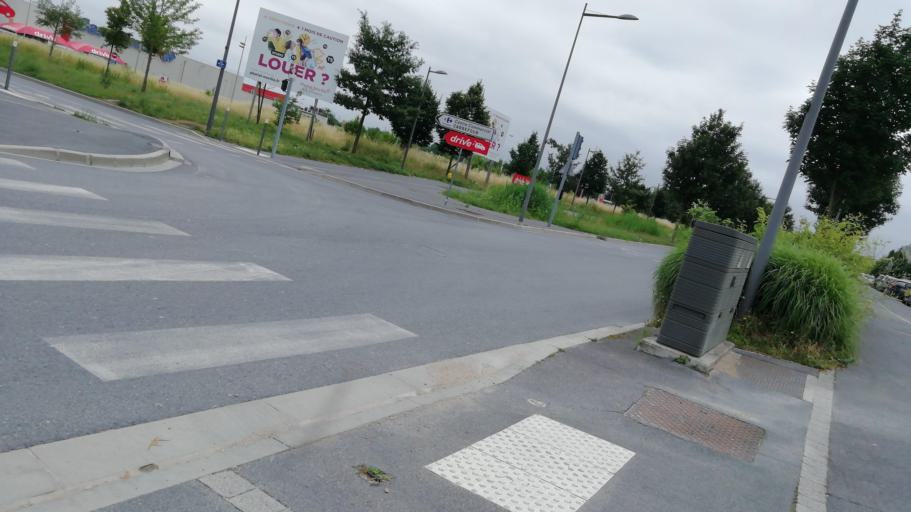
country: FR
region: Champagne-Ardenne
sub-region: Departement de la Marne
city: Betheny
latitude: 49.2614
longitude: 4.0620
